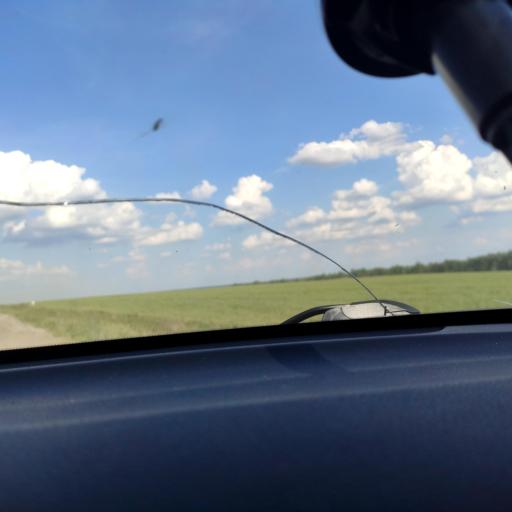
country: RU
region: Tatarstan
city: Verkhniy Uslon
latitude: 55.6448
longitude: 48.9184
